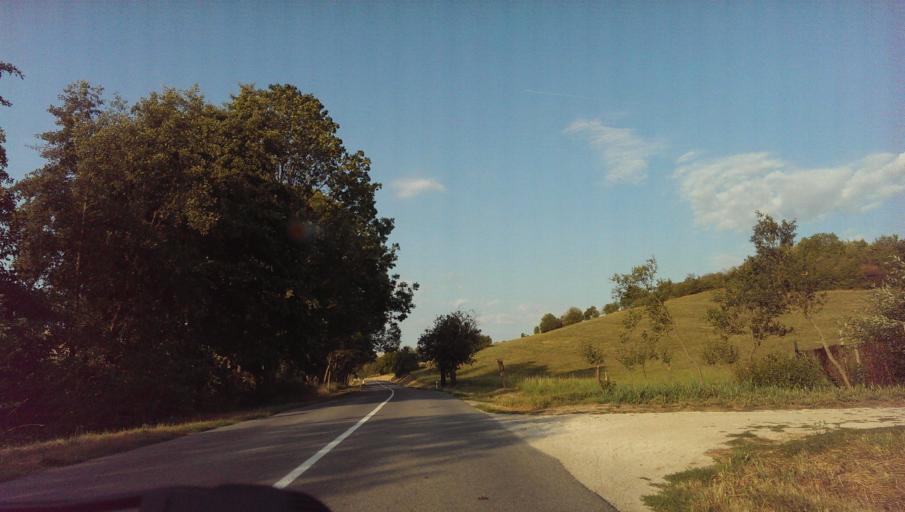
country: CZ
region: Zlin
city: Borsice
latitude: 49.0606
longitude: 17.3193
